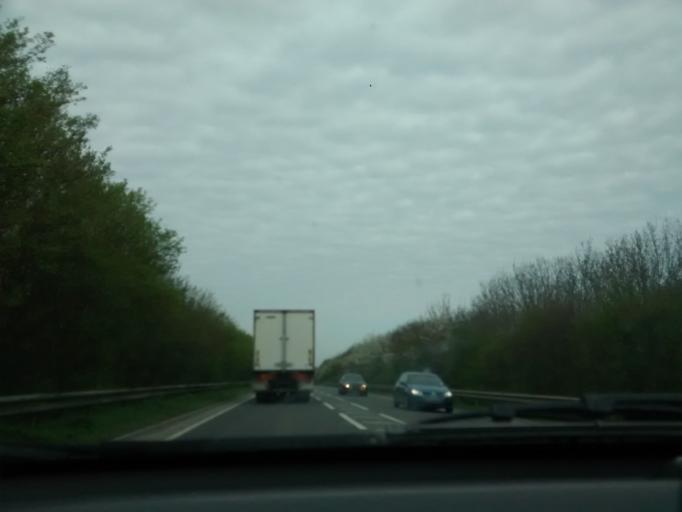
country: GB
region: England
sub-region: Oxfordshire
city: Bicester
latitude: 51.8906
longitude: -1.1544
